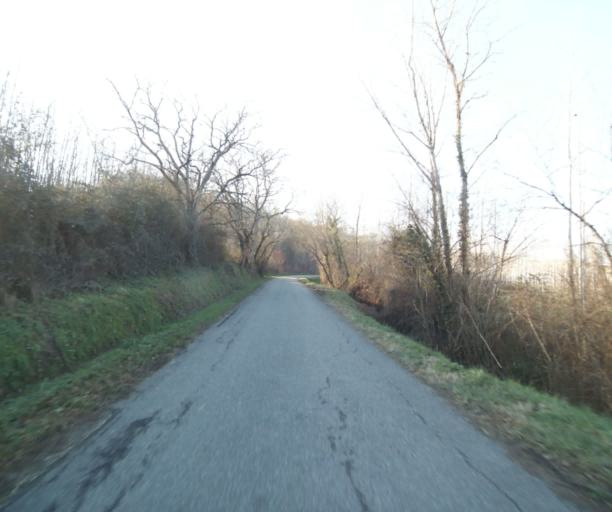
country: FR
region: Midi-Pyrenees
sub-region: Departement du Tarn-et-Garonne
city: Moissac
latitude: 44.1256
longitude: 1.0969
